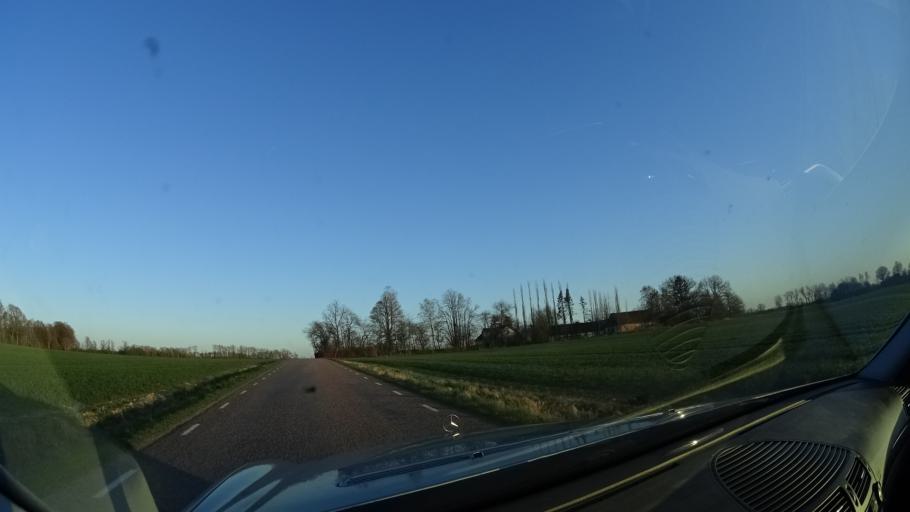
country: SE
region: Skane
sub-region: Eslovs Kommun
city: Stehag
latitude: 55.8929
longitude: 13.4215
